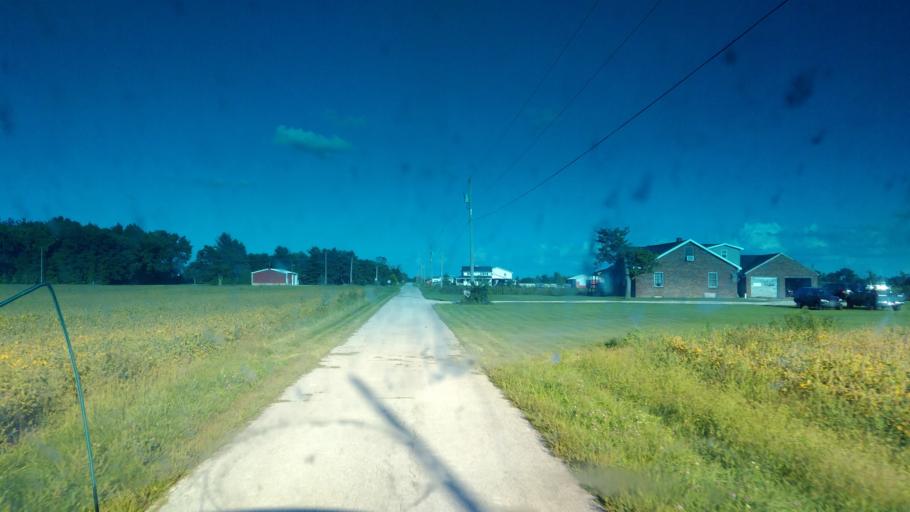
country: US
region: Ohio
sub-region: Wyandot County
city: Carey
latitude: 40.9412
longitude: -83.4504
